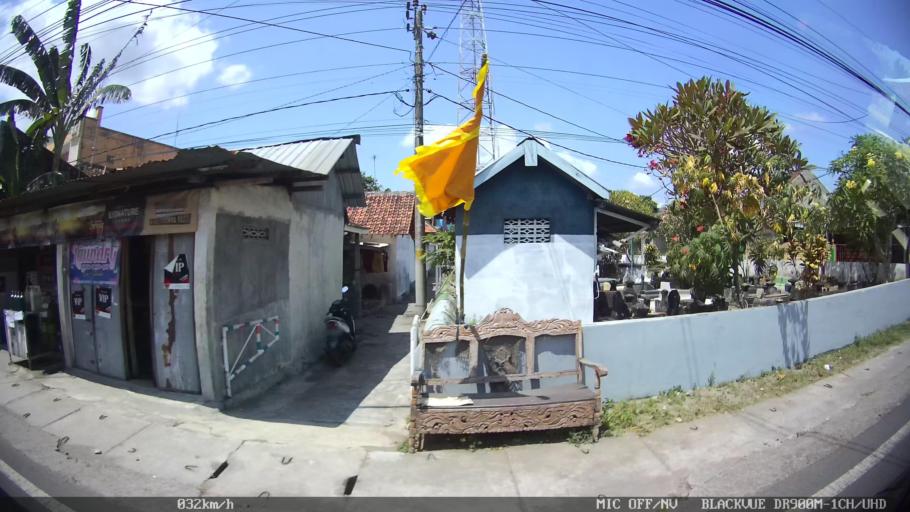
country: ID
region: Daerah Istimewa Yogyakarta
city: Pundong
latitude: -7.9188
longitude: 110.3819
